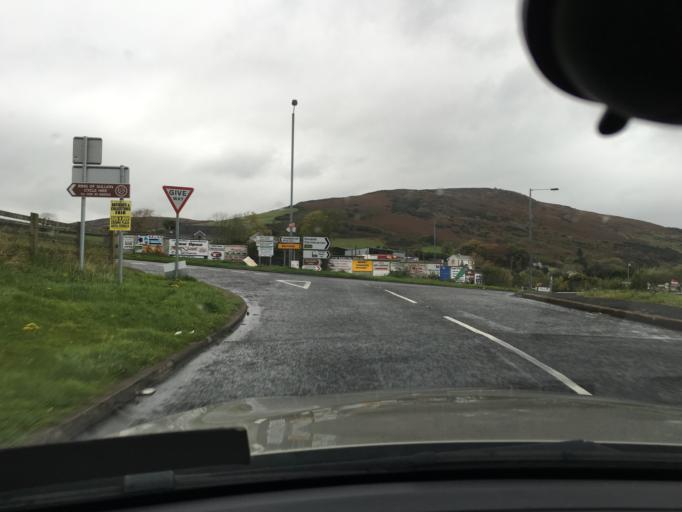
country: GB
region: Northern Ireland
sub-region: Newry and Mourne District
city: Newry
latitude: 54.0968
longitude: -6.3634
